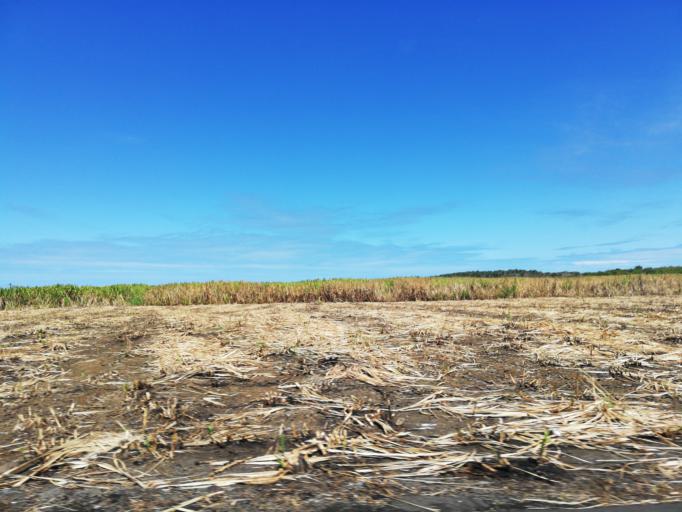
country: MU
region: Grand Port
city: Beau Vallon
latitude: -20.4446
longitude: 57.6936
